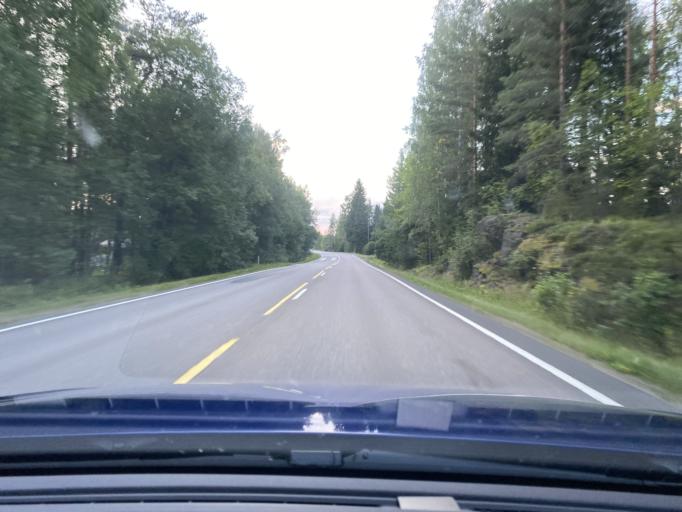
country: FI
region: Satakunta
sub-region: Pohjois-Satakunta
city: Honkajoki
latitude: 61.9359
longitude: 22.2395
